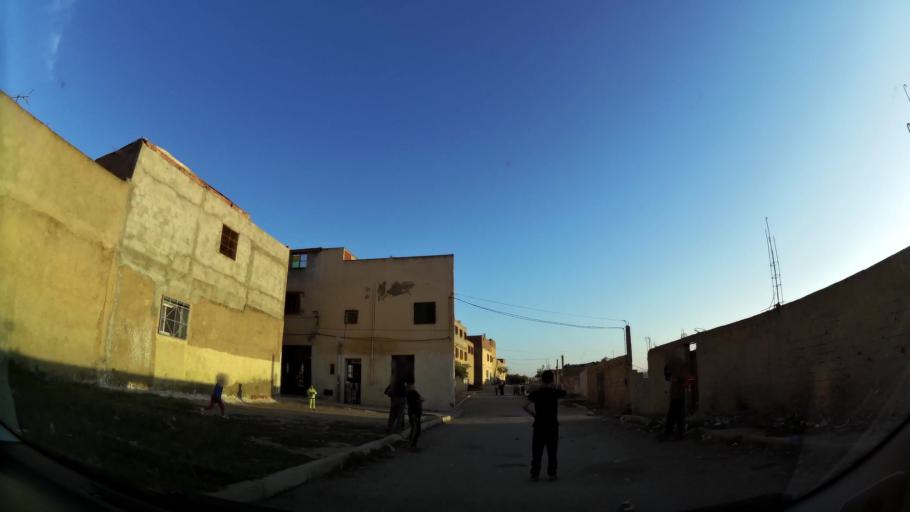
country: MA
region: Oriental
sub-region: Oujda-Angad
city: Oujda
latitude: 34.7045
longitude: -1.9237
